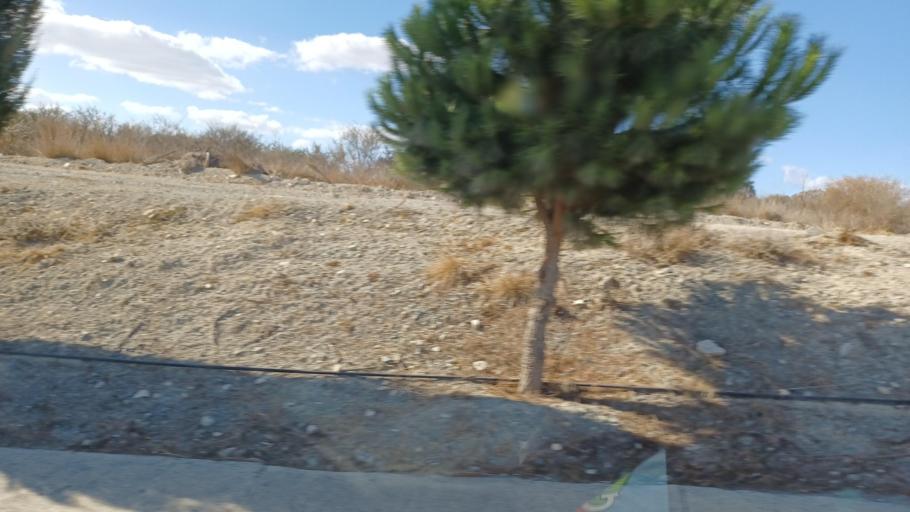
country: CY
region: Limassol
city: Pyrgos
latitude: 34.7636
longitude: 33.2298
